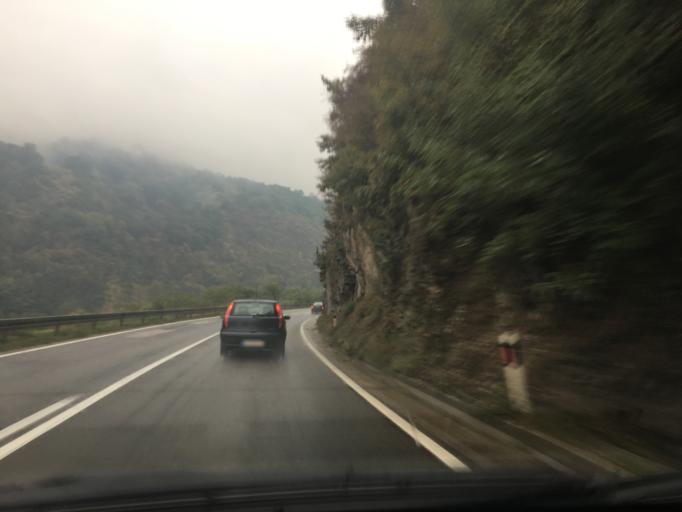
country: RS
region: Central Serbia
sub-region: Pcinjski Okrug
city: Vladicin Han
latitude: 42.7346
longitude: 22.0604
